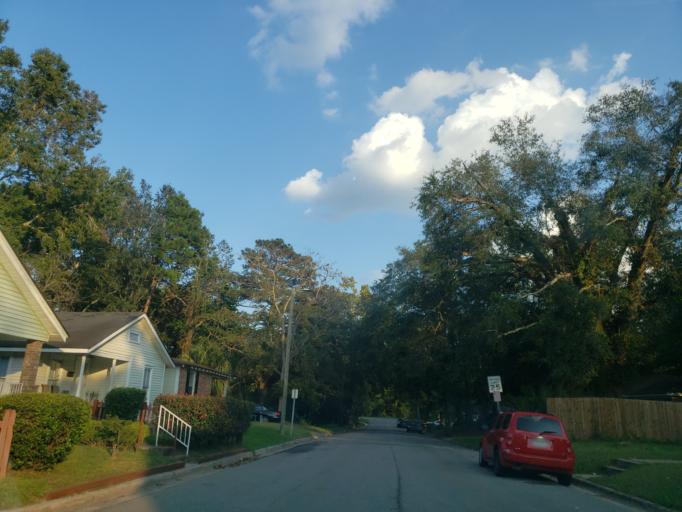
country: US
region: Georgia
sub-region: Chatham County
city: Thunderbolt
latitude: 32.0541
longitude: -81.0757
